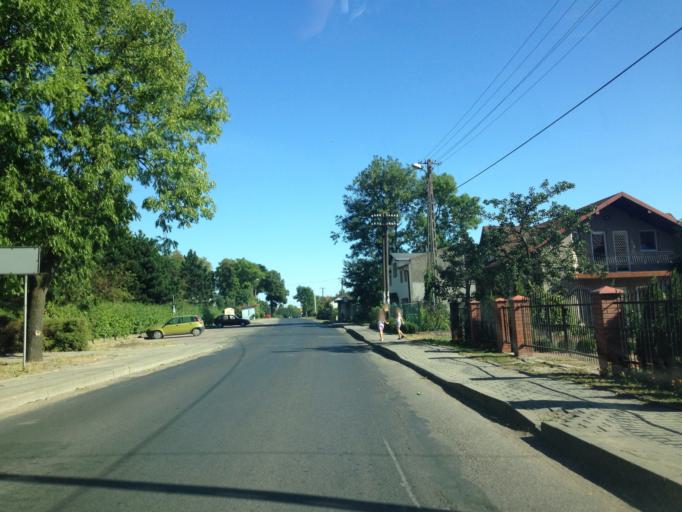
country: PL
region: Kujawsko-Pomorskie
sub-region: Powiat brodnicki
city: Brodnica
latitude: 53.2124
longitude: 19.4444
